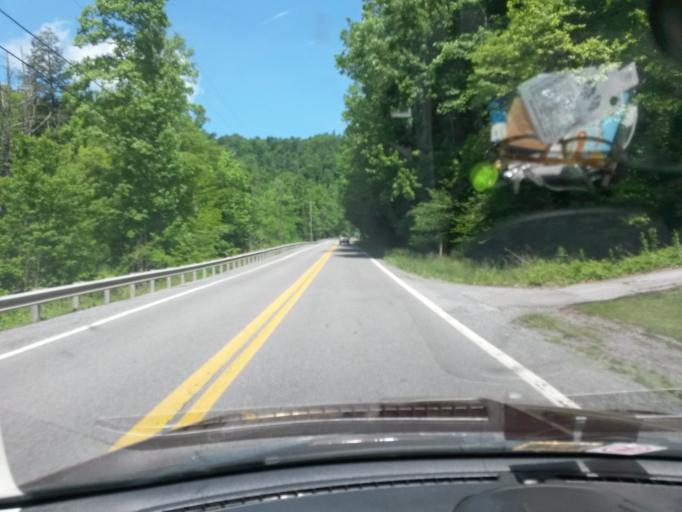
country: US
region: West Virginia
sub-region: McDowell County
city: Welch
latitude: 37.4787
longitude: -81.5446
